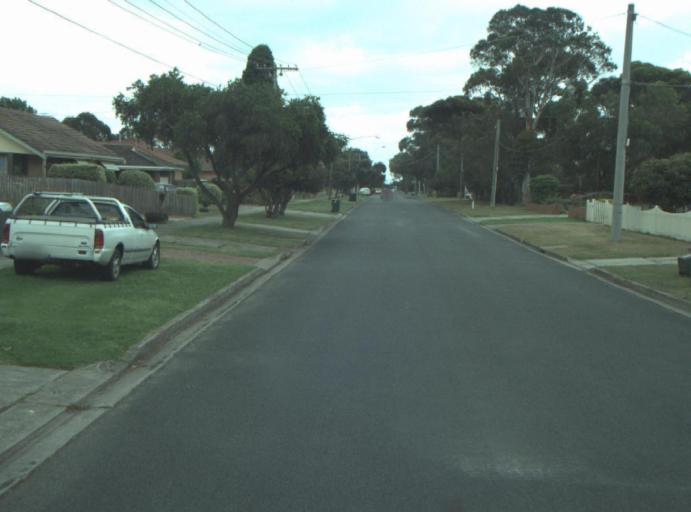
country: AU
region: Victoria
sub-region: Greater Geelong
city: East Geelong
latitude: -38.1678
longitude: 144.3996
